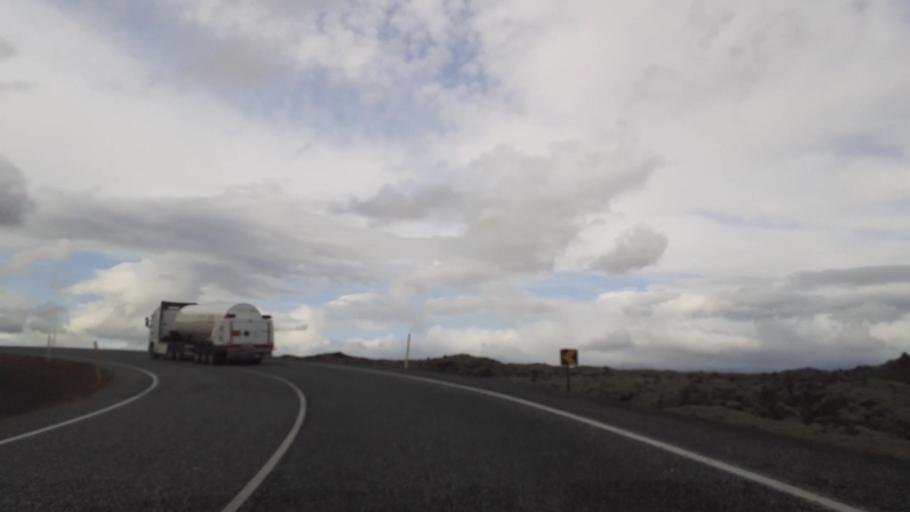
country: IS
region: South
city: THorlakshoefn
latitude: 64.0399
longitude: -21.4540
